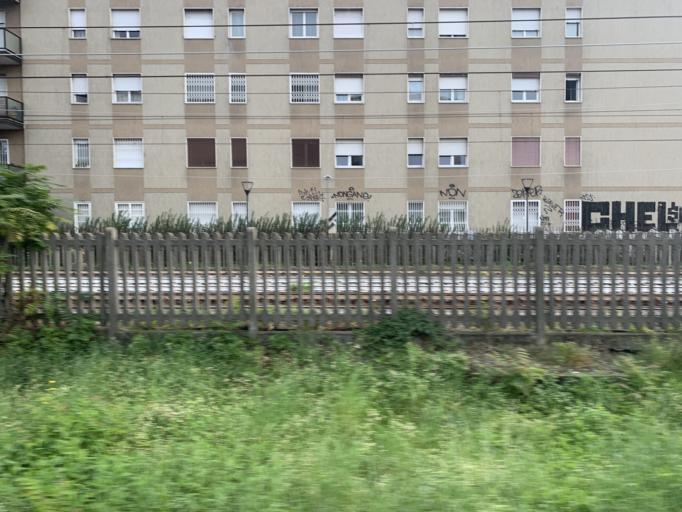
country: IT
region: Lombardy
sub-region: Citta metropolitana di Milano
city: Sesto San Giovanni
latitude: 45.5031
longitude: 9.2455
